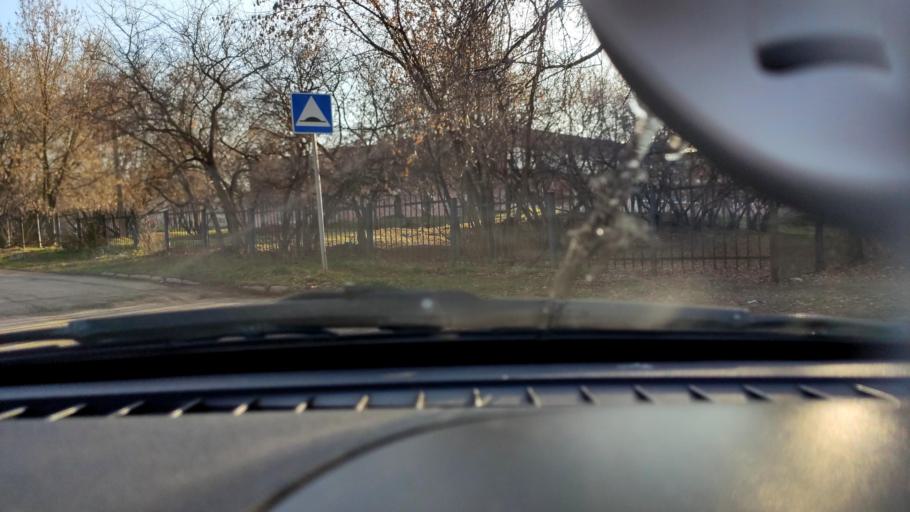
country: RU
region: Perm
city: Perm
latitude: 57.9771
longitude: 56.2331
